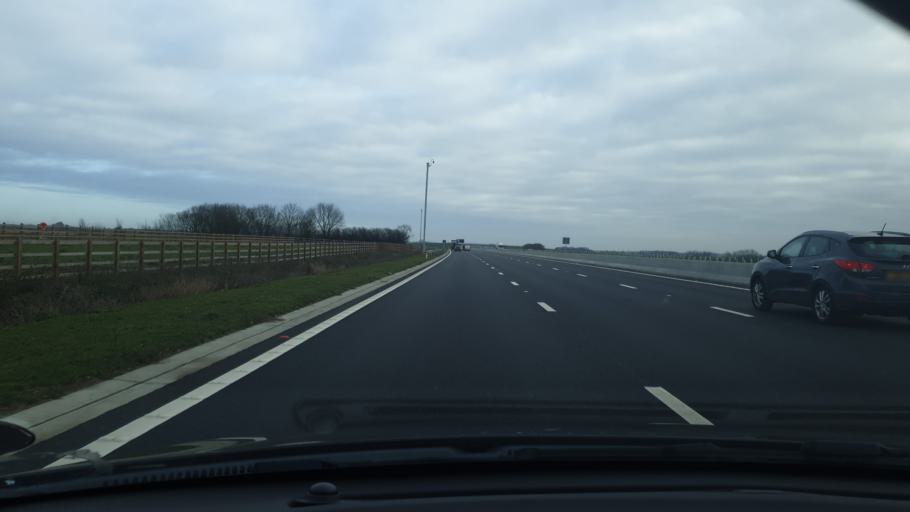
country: GB
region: England
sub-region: Cambridgeshire
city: Hemingford Grey
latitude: 52.2925
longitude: -0.1367
